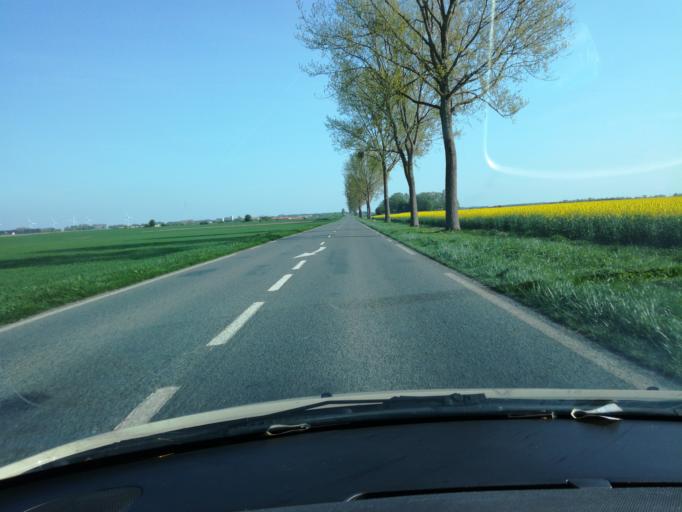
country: FR
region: Picardie
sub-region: Departement de la Somme
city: Poix-de-Picardie
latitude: 49.8183
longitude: 1.9585
